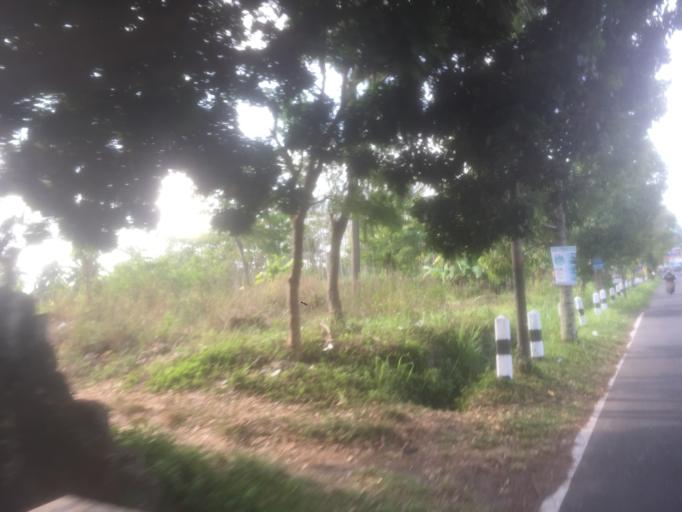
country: ID
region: Daerah Istimewa Yogyakarta
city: Sleman
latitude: -7.6489
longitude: 110.4239
